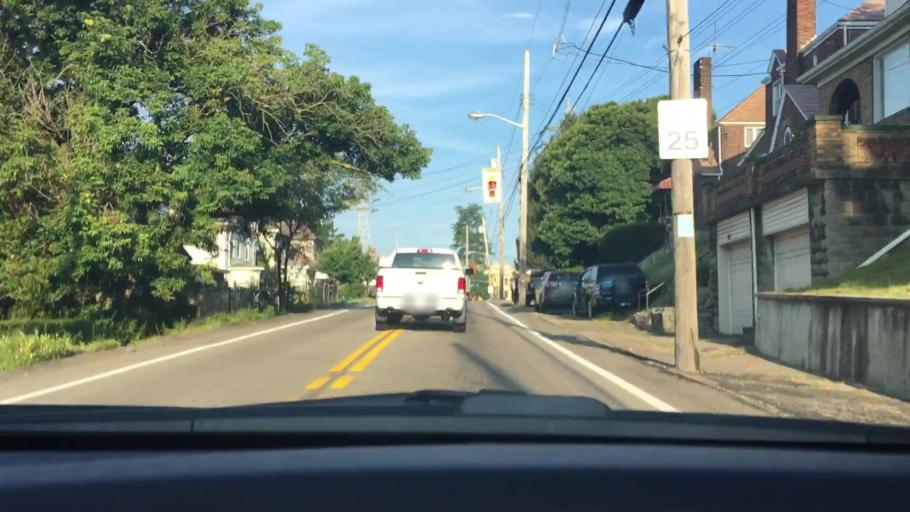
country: US
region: Pennsylvania
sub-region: Allegheny County
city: West Homestead
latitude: 40.3695
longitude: -79.9113
